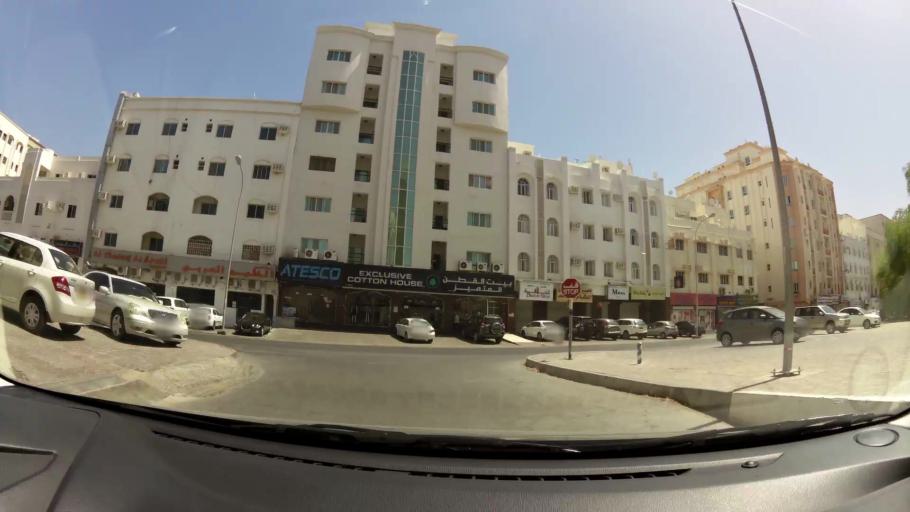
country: OM
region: Muhafazat Masqat
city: Bawshar
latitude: 23.5916
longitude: 58.4006
